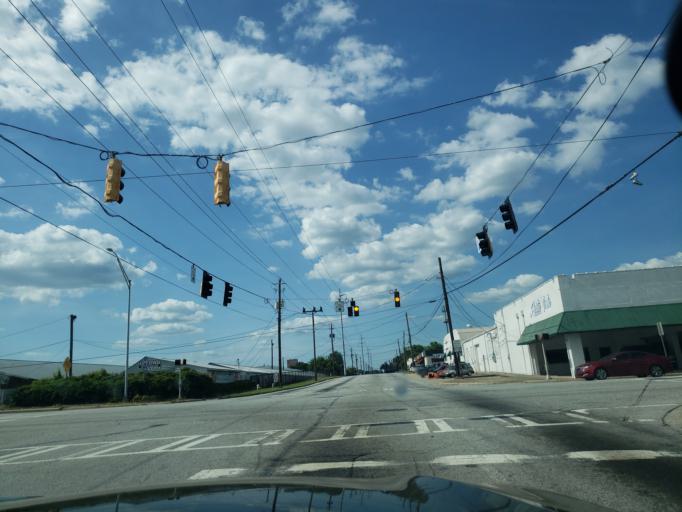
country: US
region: Georgia
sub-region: Muscogee County
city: Columbus
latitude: 32.4703
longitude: -84.9798
